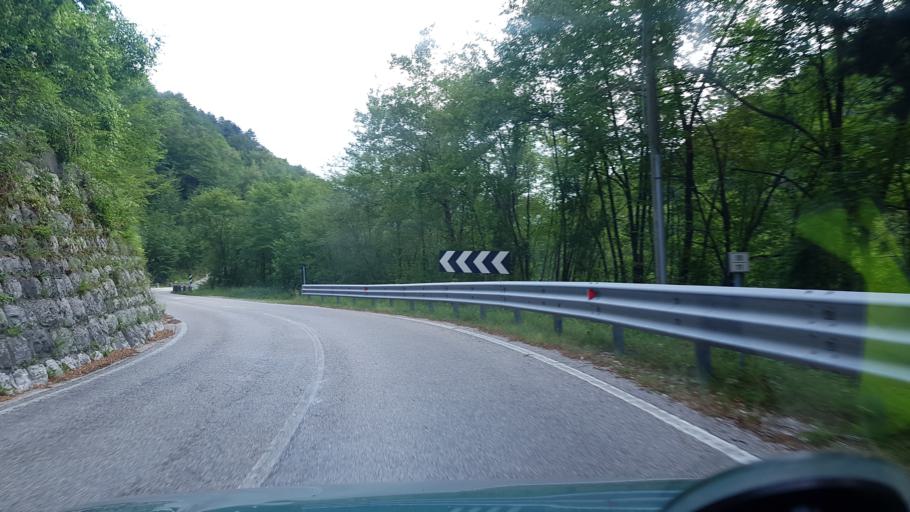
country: IT
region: Friuli Venezia Giulia
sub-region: Provincia di Udine
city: Lusevera
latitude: 46.2978
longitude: 13.2700
